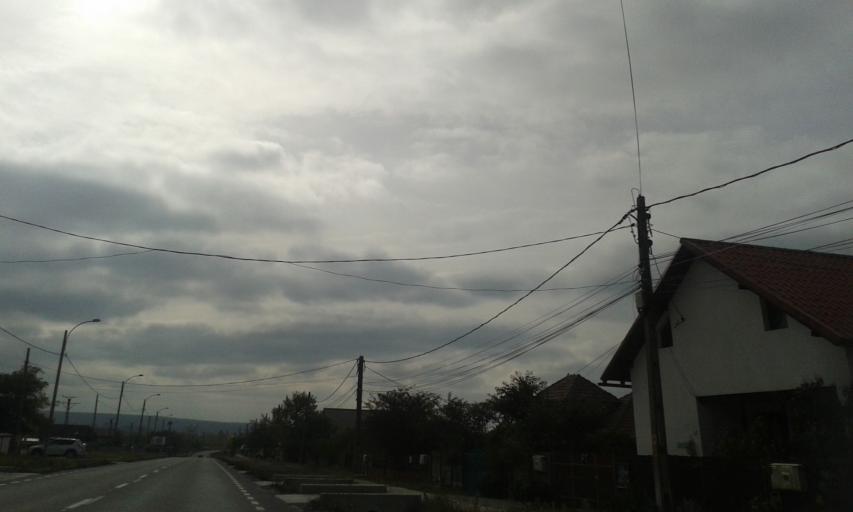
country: RO
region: Gorj
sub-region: Comuna Bumbesti-Jiu
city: Bumbesti-Jiu
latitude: 45.1719
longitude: 23.3813
